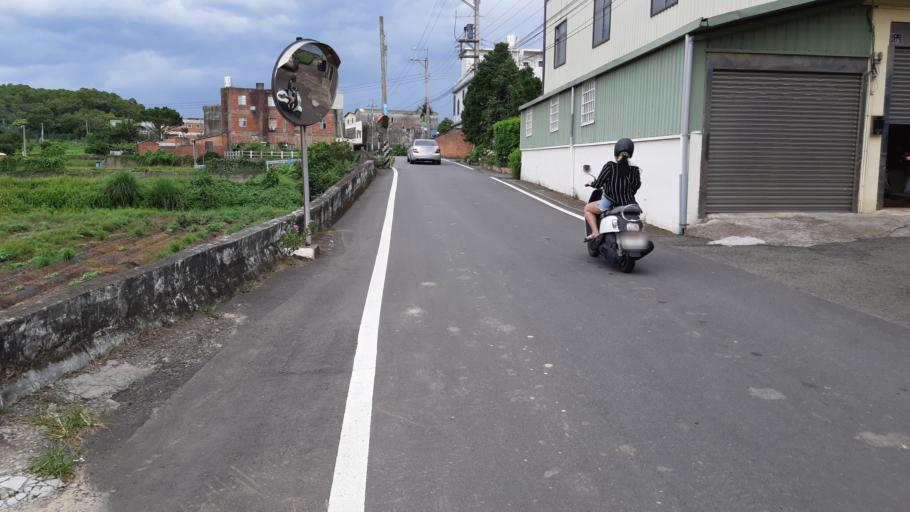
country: TW
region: Taiwan
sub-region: Miaoli
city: Miaoli
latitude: 24.6579
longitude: 120.8878
